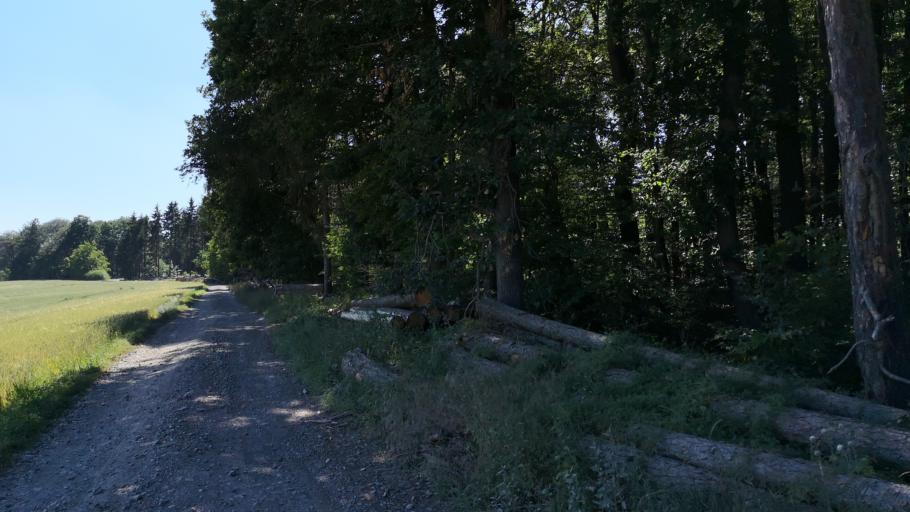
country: DE
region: Saxony-Anhalt
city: Uftrungen
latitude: 51.5382
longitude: 11.0476
